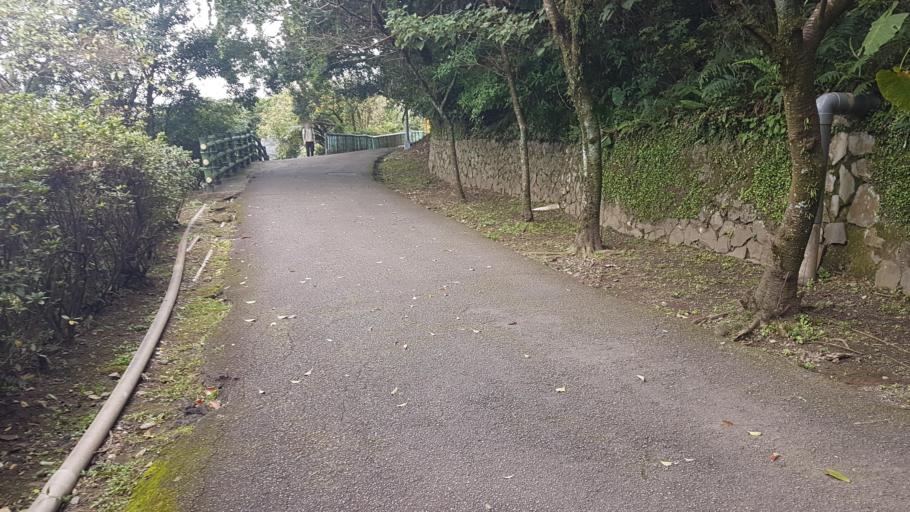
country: TW
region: Taipei
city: Taipei
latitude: 25.1538
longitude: 121.5392
